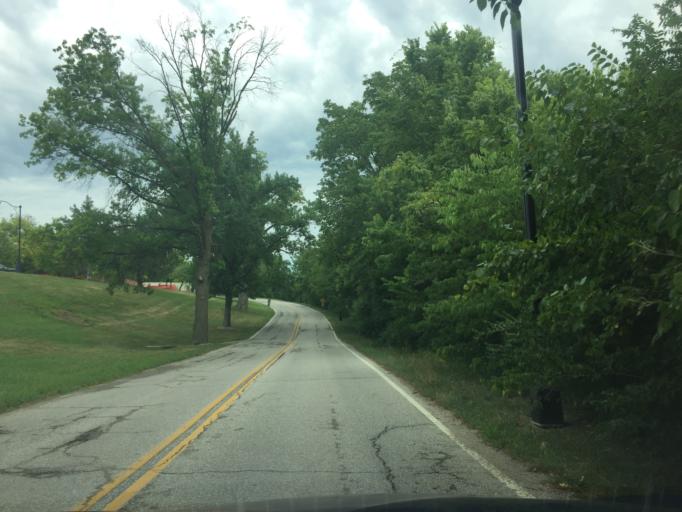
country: US
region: Kansas
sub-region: Leavenworth County
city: Leavenworth
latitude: 39.3469
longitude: -94.9128
